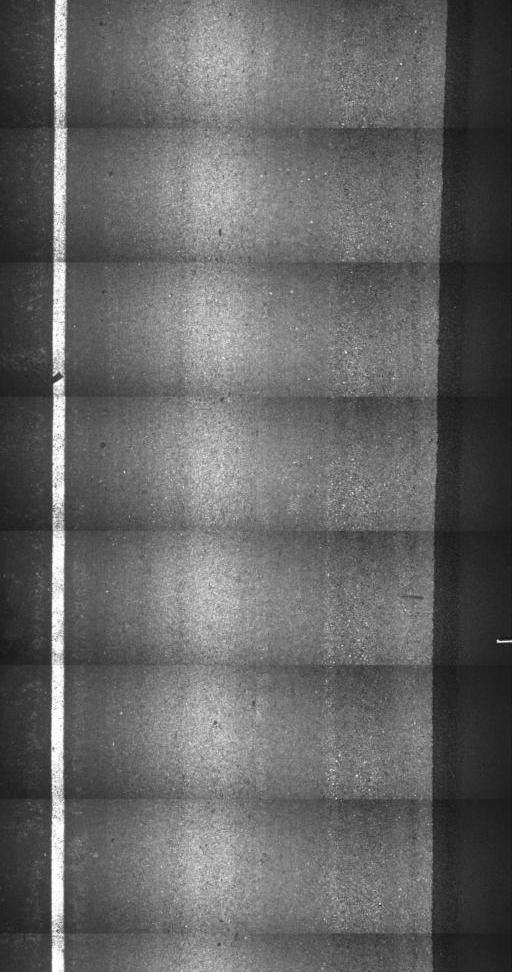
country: US
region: Vermont
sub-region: Franklin County
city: Richford
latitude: 44.9766
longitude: -72.5198
